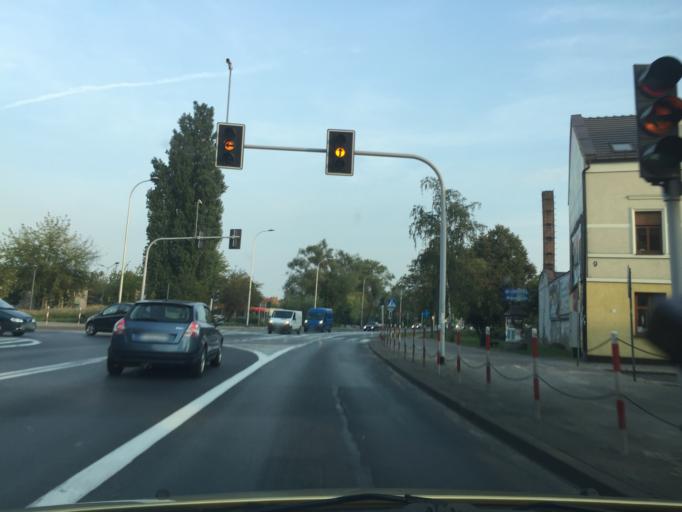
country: PL
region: Greater Poland Voivodeship
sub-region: Powiat jarocinski
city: Jarocin
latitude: 51.9732
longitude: 17.5030
